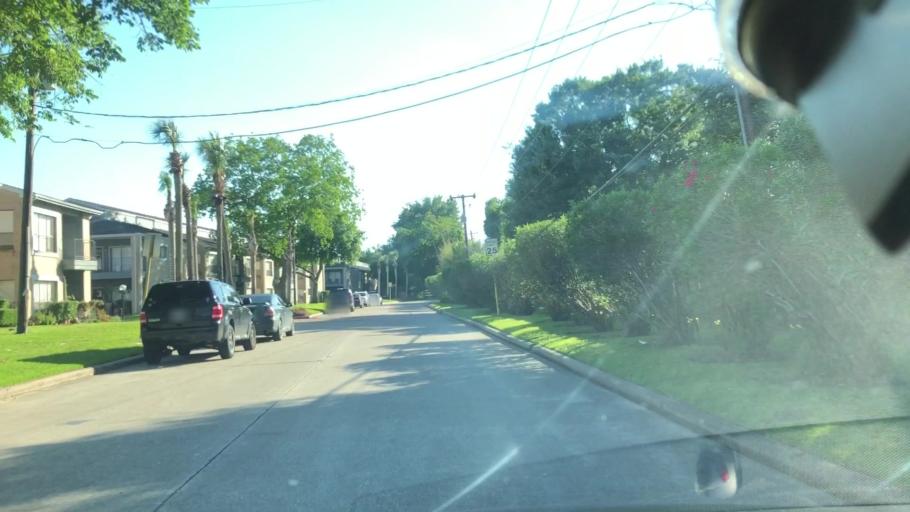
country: US
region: Texas
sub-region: Harris County
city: Nassau Bay
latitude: 29.5372
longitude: -95.1004
